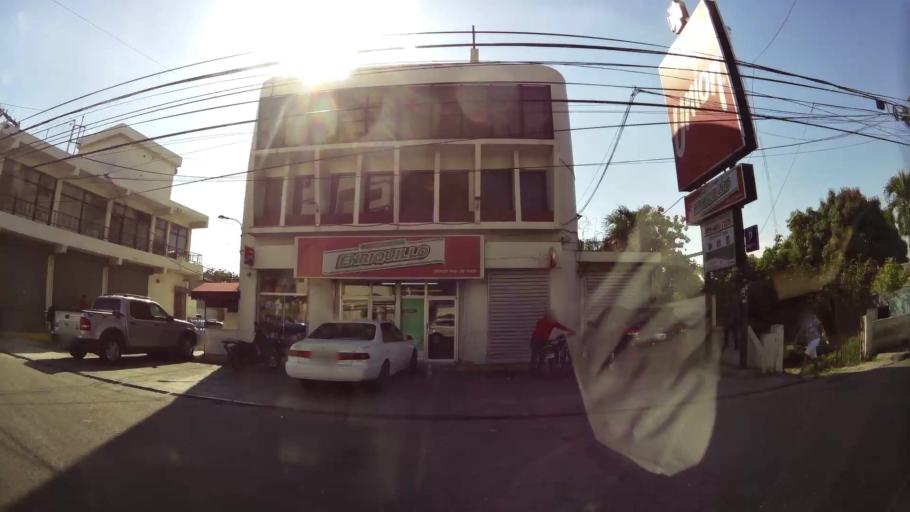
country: DO
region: Nacional
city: Santo Domingo
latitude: 18.4774
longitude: -69.9719
